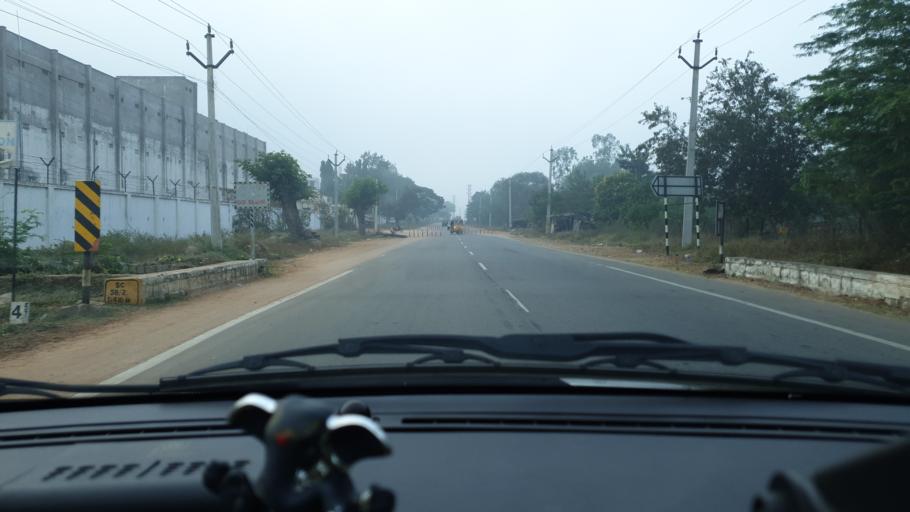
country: IN
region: Telangana
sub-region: Mahbubnagar
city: Farrukhnagar
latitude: 16.8725
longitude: 78.5293
